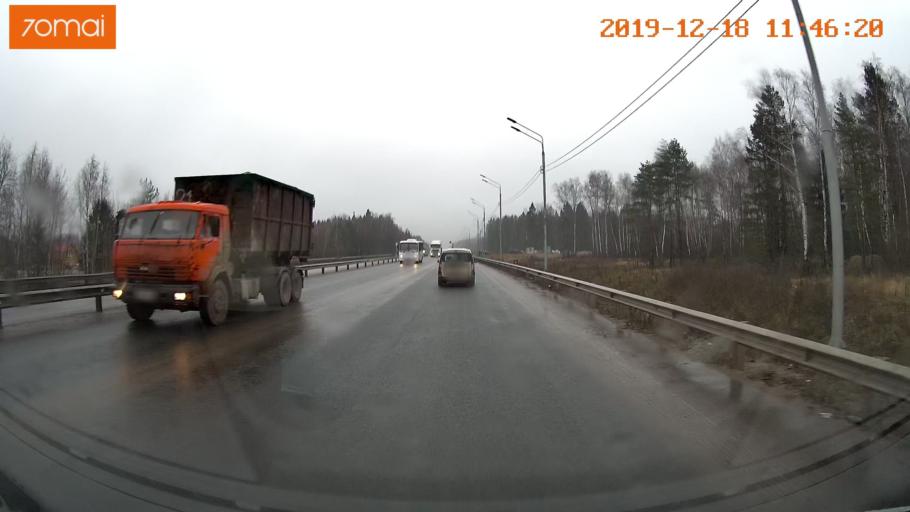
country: RU
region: Moskovskaya
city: Zvenigorod
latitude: 55.7486
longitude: 36.8870
